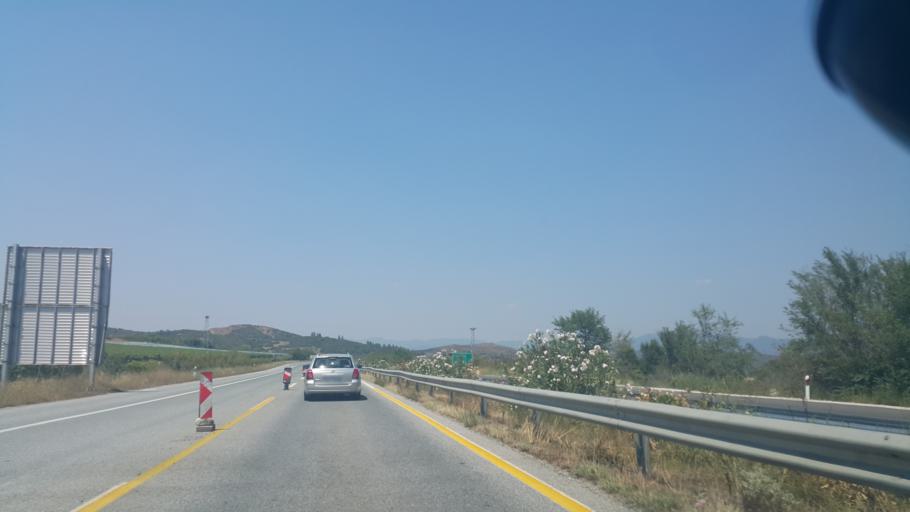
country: MK
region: Gevgelija
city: Gevgelija
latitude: 41.2138
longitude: 22.4930
